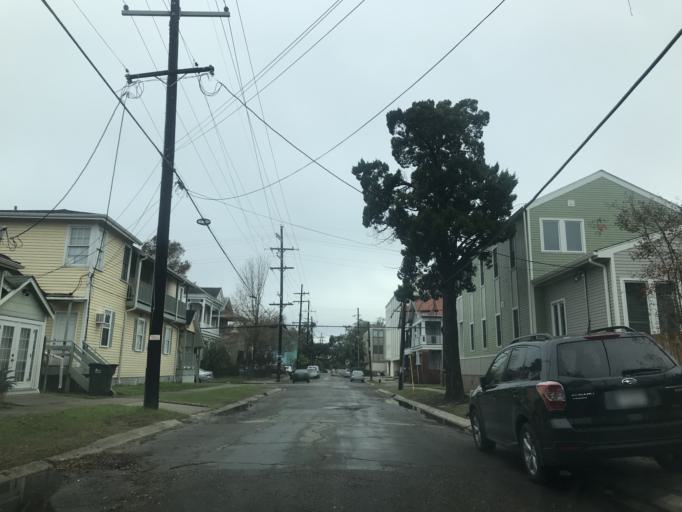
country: US
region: Louisiana
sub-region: Orleans Parish
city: New Orleans
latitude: 29.9738
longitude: -90.0965
